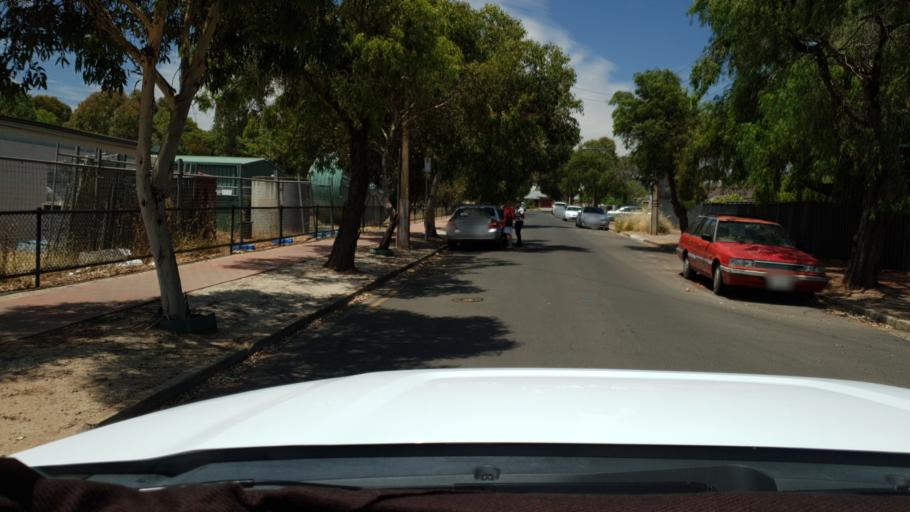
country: AU
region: South Australia
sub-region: Marion
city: Clovelly Park
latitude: -35.0077
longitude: 138.5784
